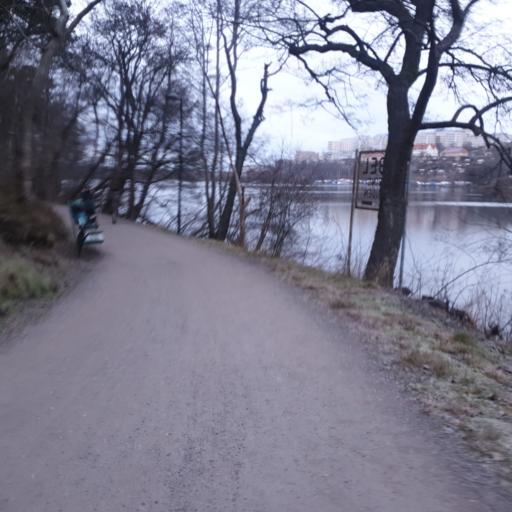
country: SE
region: Stockholm
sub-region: Stockholms Kommun
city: Arsta
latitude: 59.3024
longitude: 18.0646
